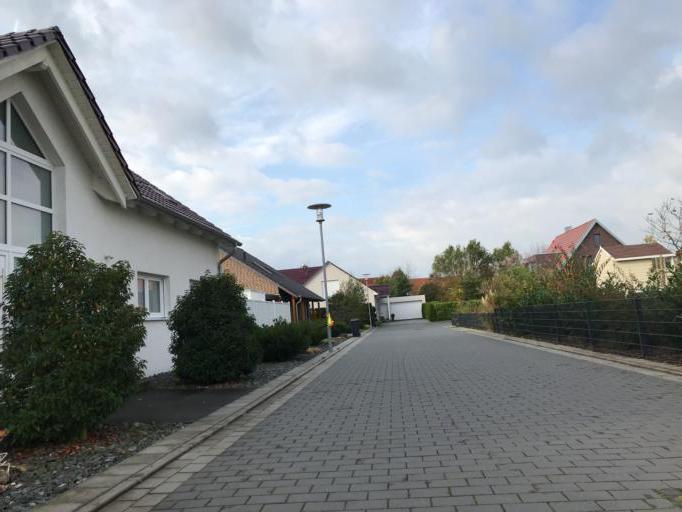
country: DE
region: Lower Saxony
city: Braunschweig
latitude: 52.2889
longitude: 10.4676
